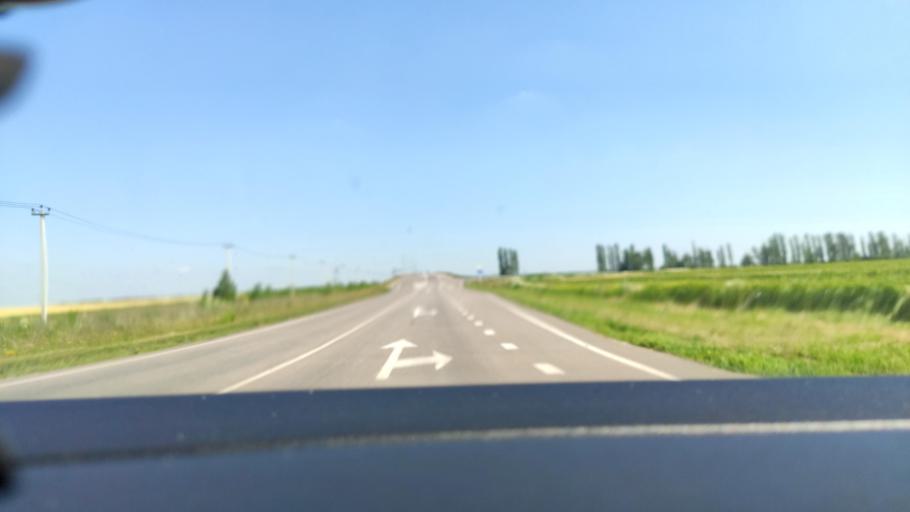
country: RU
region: Voronezj
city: Novaya Usman'
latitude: 51.5845
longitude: 39.3745
